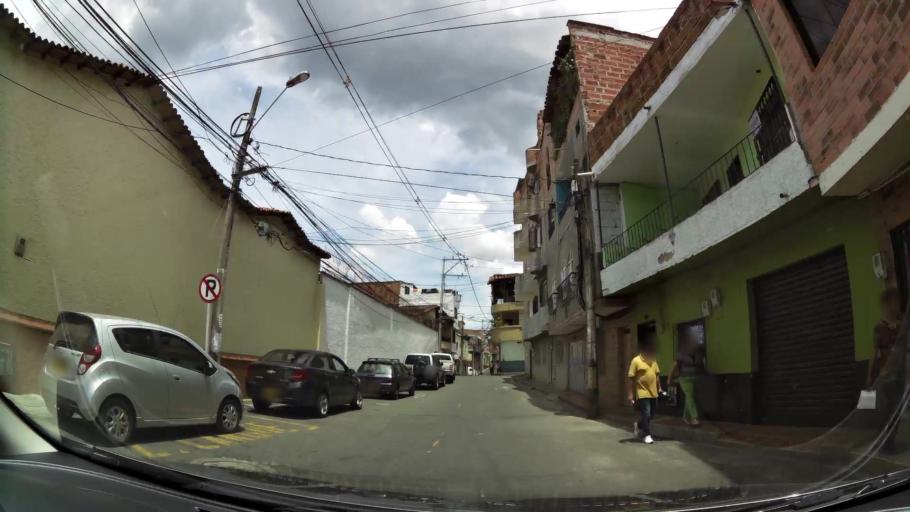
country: CO
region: Antioquia
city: Municipio de Copacabana
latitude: 6.3450
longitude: -75.5080
